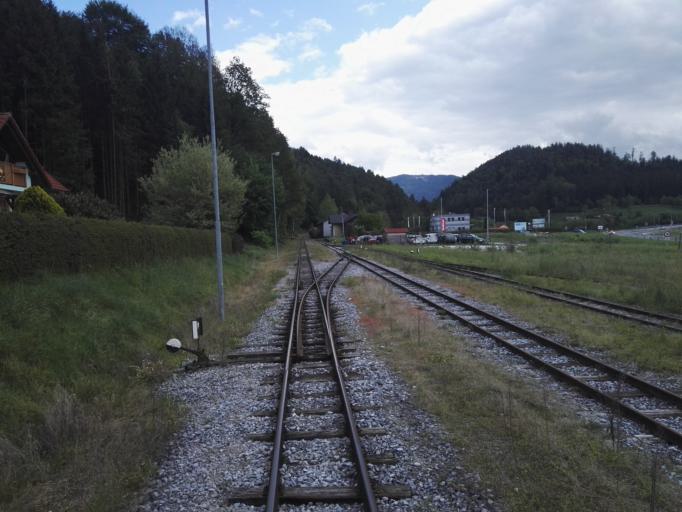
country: AT
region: Styria
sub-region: Politischer Bezirk Weiz
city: Baierdorf-Umgebung
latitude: 47.2616
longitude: 15.7132
